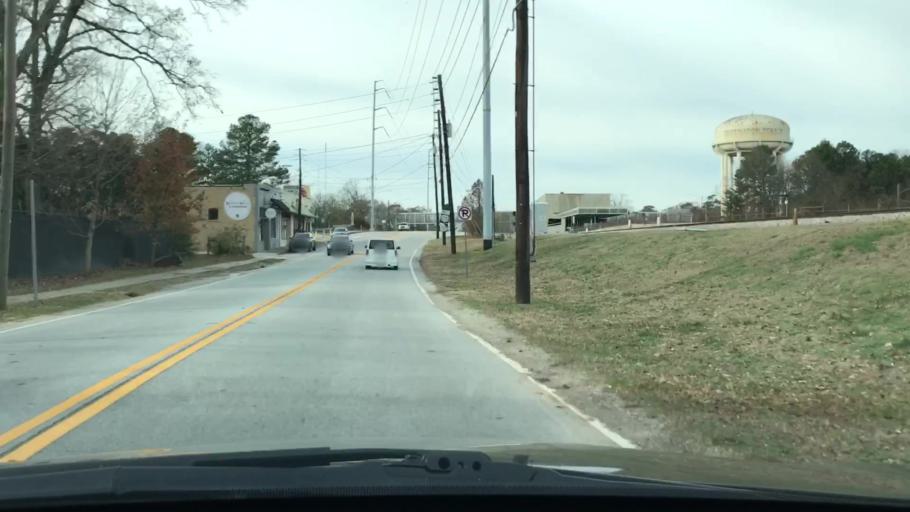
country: US
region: Georgia
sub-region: DeKalb County
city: Decatur
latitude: 33.7652
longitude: -84.3099
